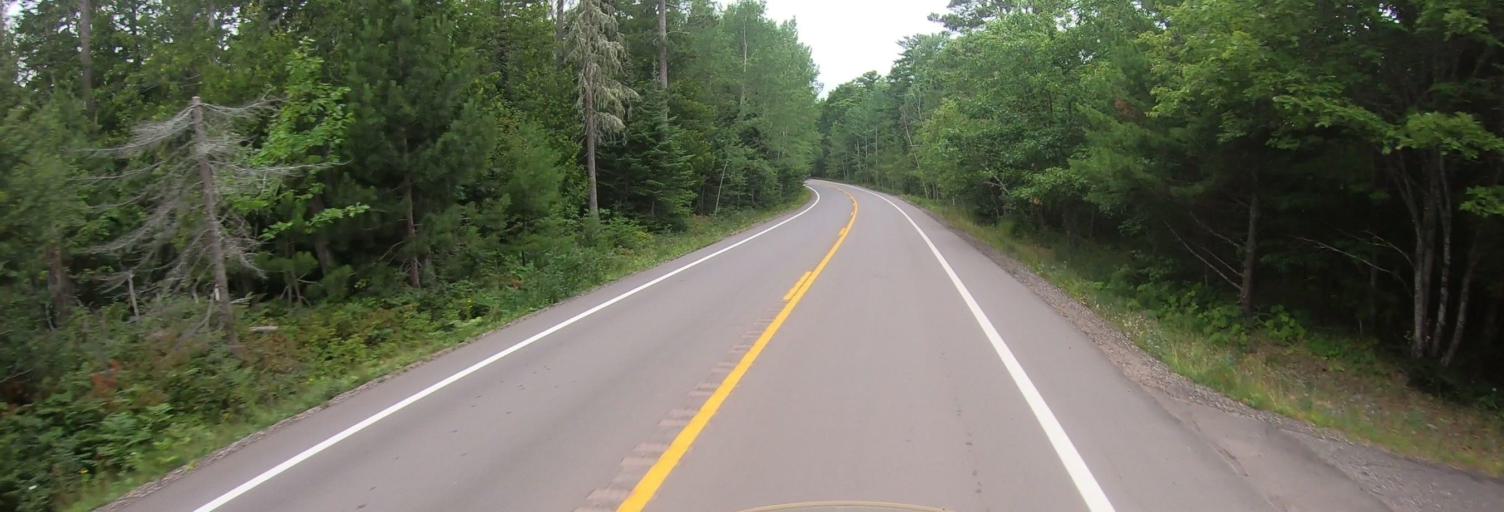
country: US
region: Michigan
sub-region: Keweenaw County
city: Eagle River
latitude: 47.4673
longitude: -87.8565
